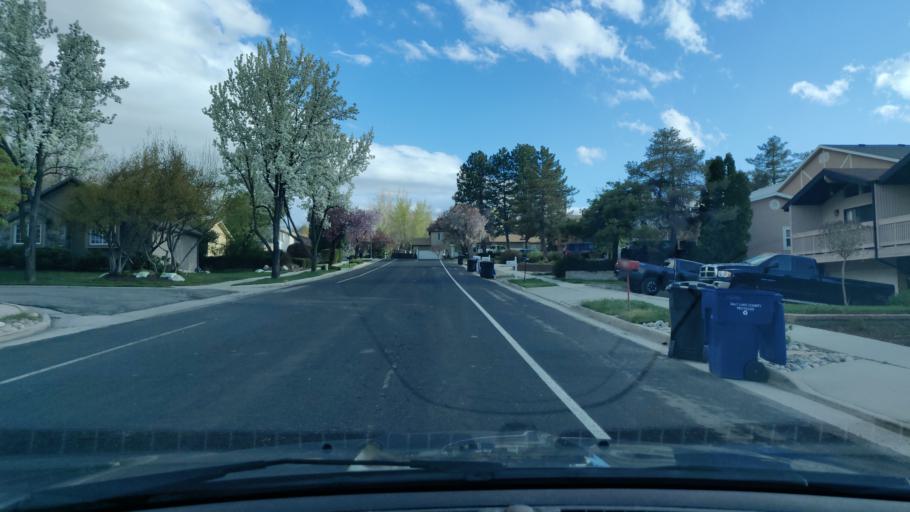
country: US
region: Utah
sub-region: Salt Lake County
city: Little Cottonwood Creek Valley
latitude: 40.6195
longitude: -111.8332
